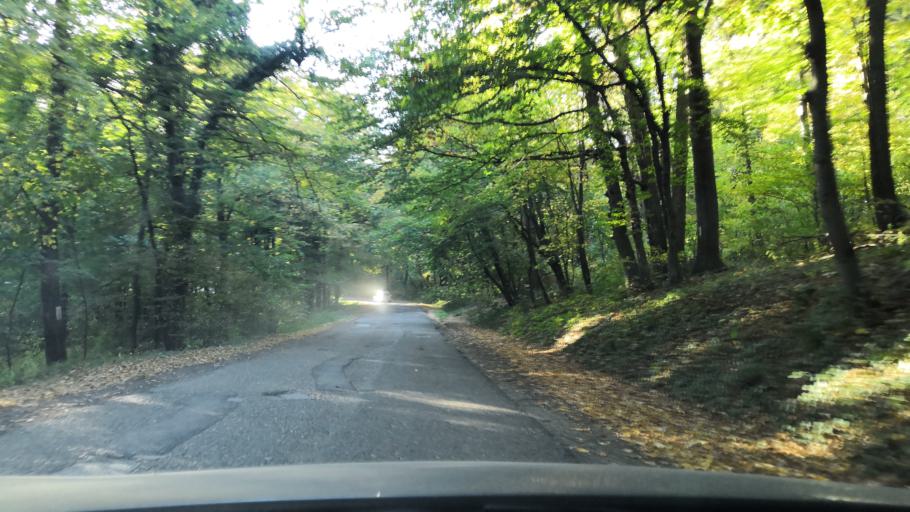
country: RS
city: Vrdnik
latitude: 45.1592
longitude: 19.7848
